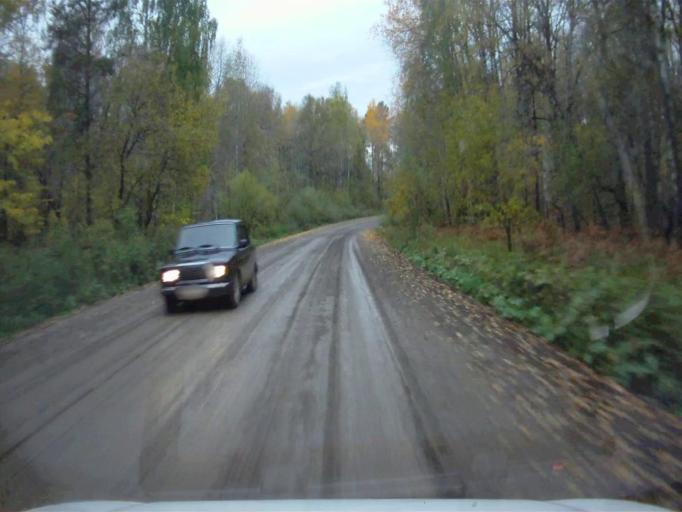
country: RU
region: Chelyabinsk
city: Nyazepetrovsk
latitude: 56.1144
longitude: 59.3684
